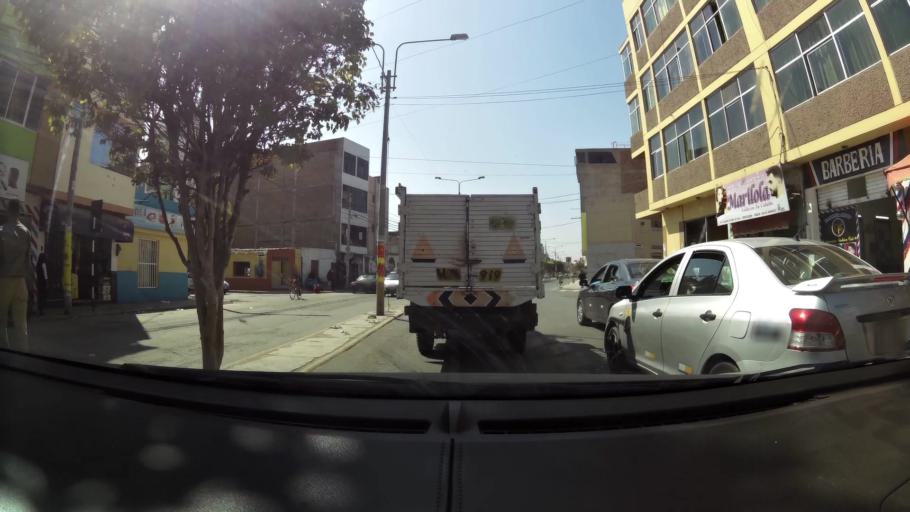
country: PE
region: Lambayeque
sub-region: Provincia de Chiclayo
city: Chiclayo
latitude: -6.7733
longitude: -79.8361
